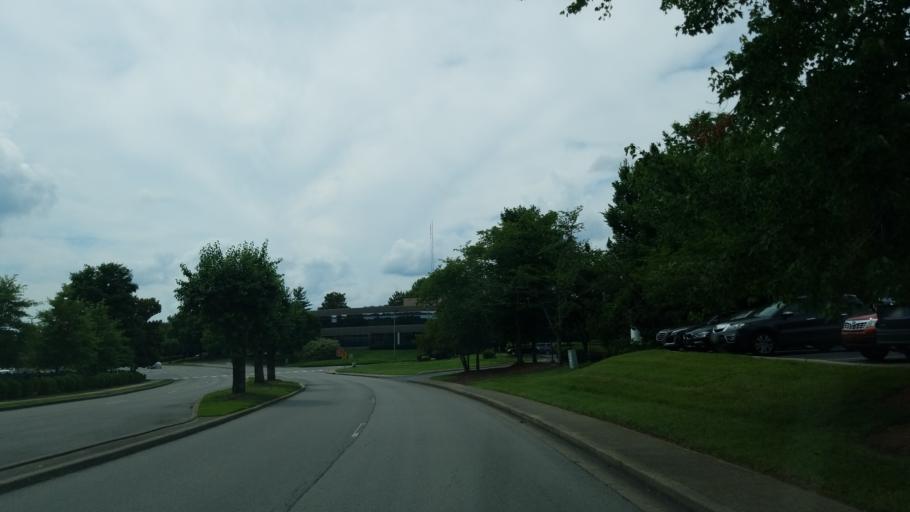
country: US
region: Tennessee
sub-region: Williamson County
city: Brentwood
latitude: 36.0336
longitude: -86.8123
